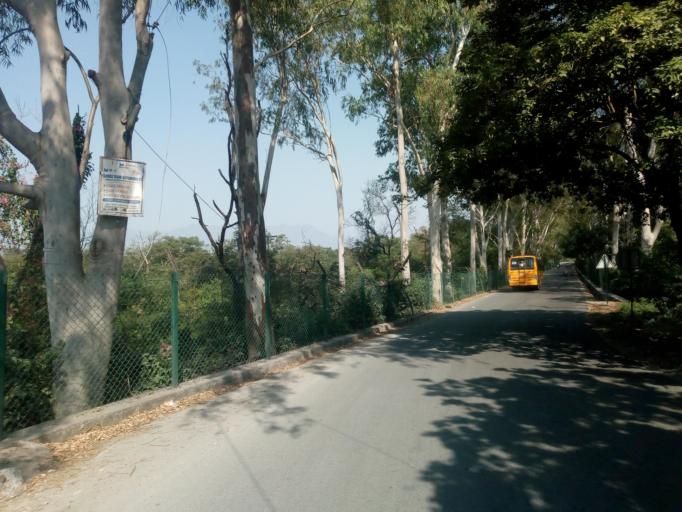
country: IN
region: Himachal Pradesh
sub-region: Sirmaur
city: Paonta Sahib
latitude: 30.4376
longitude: 77.6659
